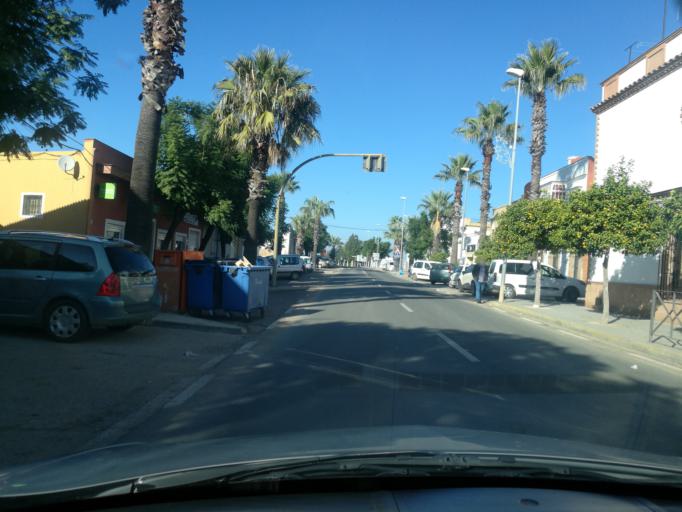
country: ES
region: Andalusia
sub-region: Provincia de Sevilla
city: La Campana
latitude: 37.5697
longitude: -5.4300
